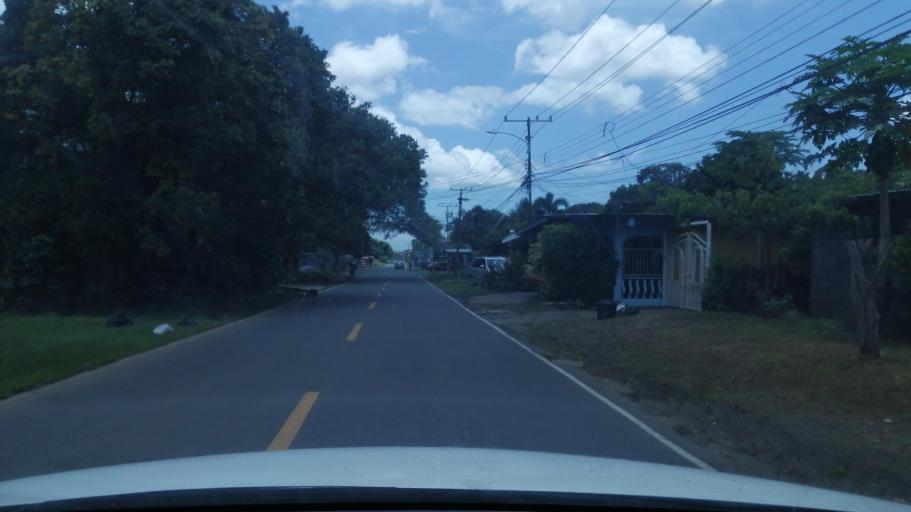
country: PA
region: Chiriqui
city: David
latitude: 8.4326
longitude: -82.4320
